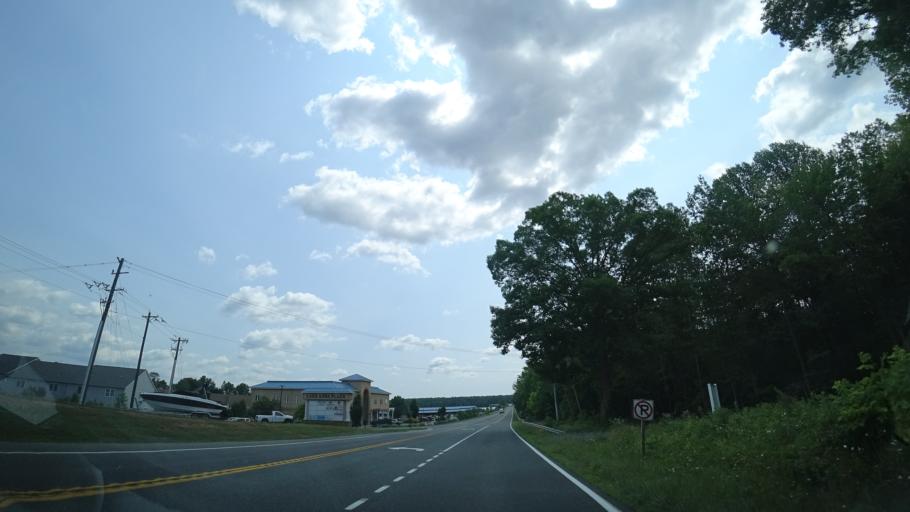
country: US
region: Virginia
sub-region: Louisa County
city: Louisa
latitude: 38.0847
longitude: -77.8250
